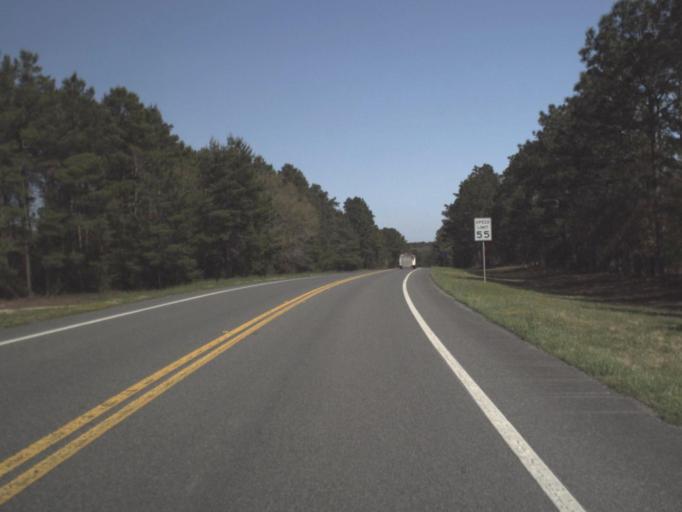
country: US
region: Florida
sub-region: Walton County
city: DeFuniak Springs
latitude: 30.7228
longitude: -86.0329
